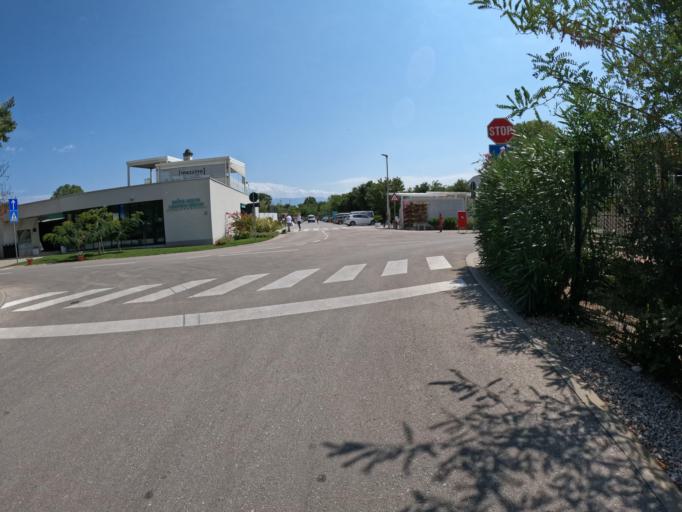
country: HR
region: Primorsko-Goranska
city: Punat
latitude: 44.9667
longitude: 14.7449
